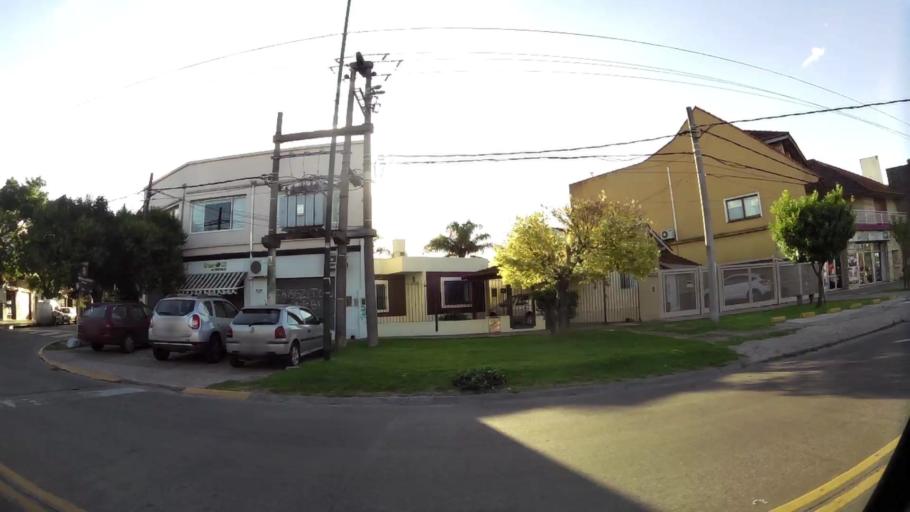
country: AR
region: Buenos Aires
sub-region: Partido de San Isidro
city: San Isidro
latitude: -34.4736
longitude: -58.5557
